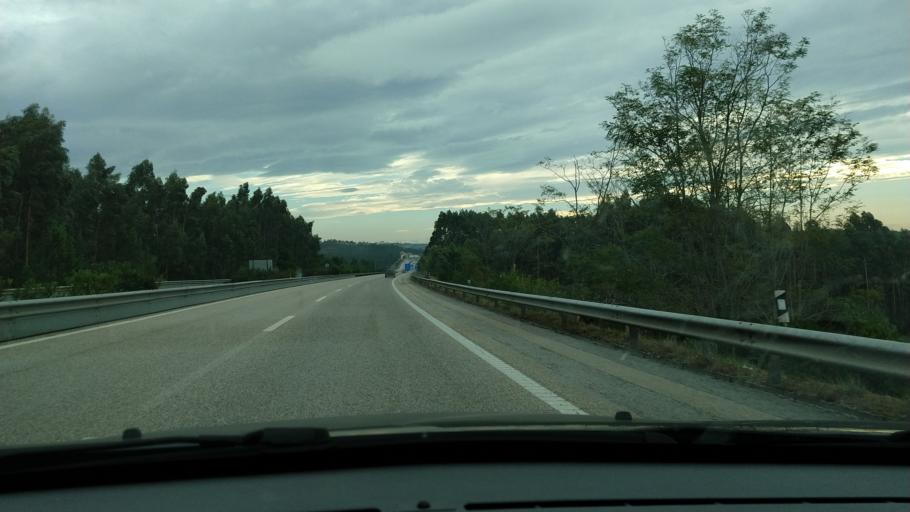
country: PT
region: Coimbra
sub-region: Figueira da Foz
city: Alhadas
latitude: 40.1535
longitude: -8.8032
